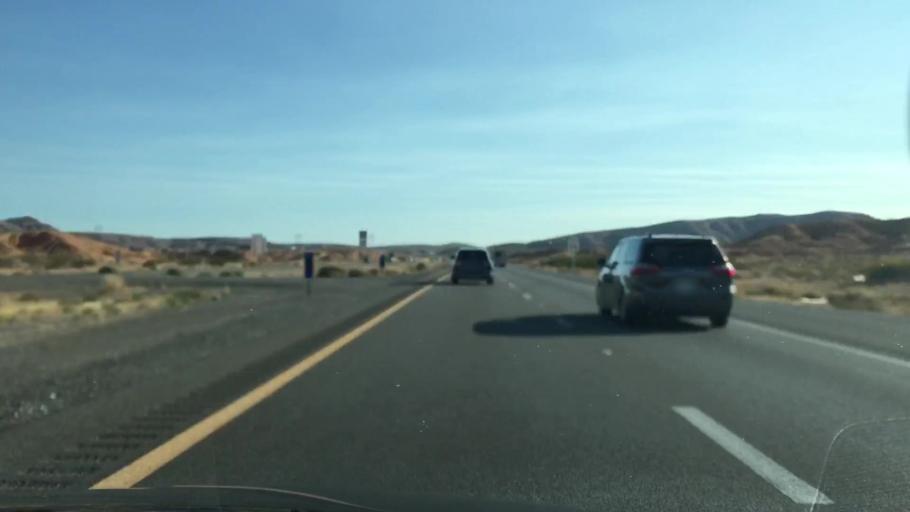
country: US
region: Nevada
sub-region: Clark County
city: Moapa Town
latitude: 36.6657
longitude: -114.5539
